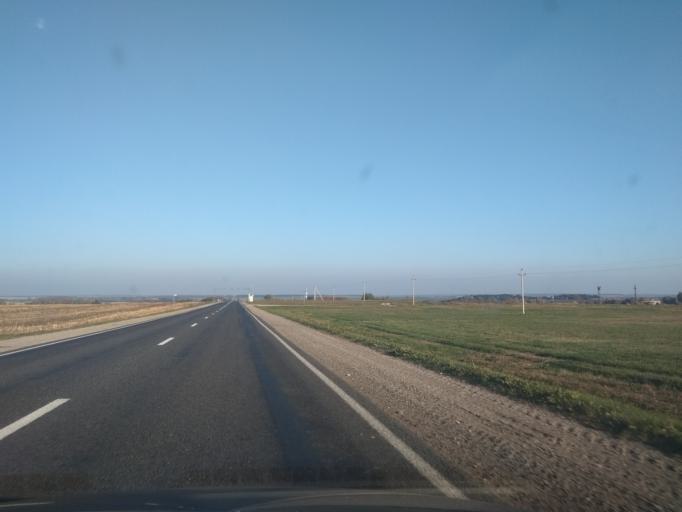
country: BY
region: Grodnenskaya
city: Svislach
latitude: 53.1311
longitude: 24.1835
